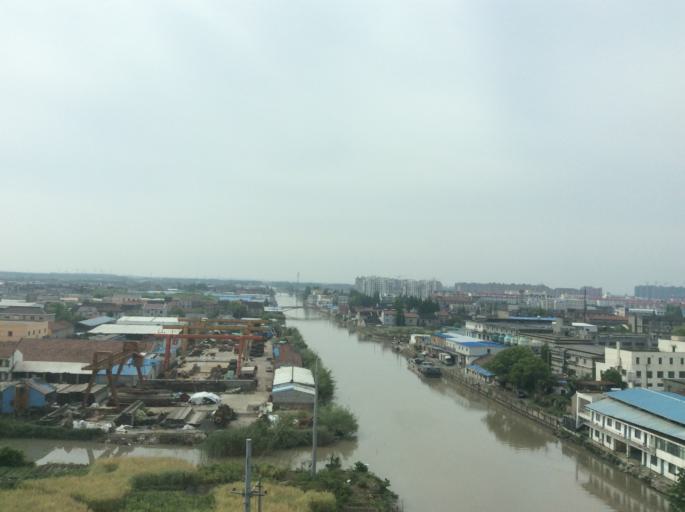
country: CN
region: Shanghai Shi
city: Kangqiao
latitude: 31.2032
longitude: 121.7039
